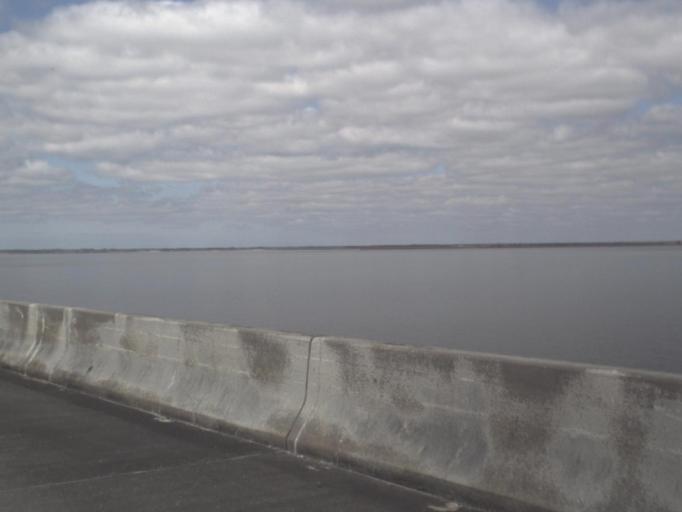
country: US
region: Florida
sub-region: Franklin County
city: Eastpoint
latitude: 29.7323
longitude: -84.9236
